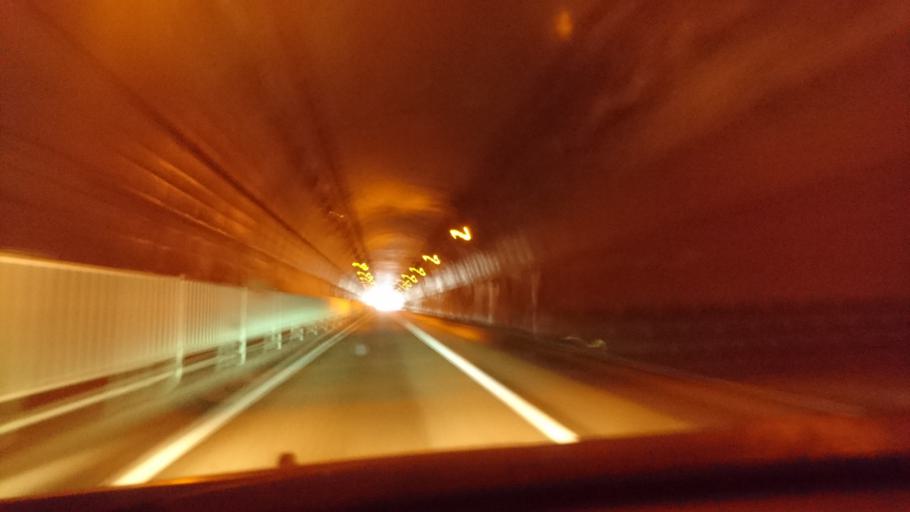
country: JP
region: Iwate
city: Kamaishi
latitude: 39.2095
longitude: 141.8729
